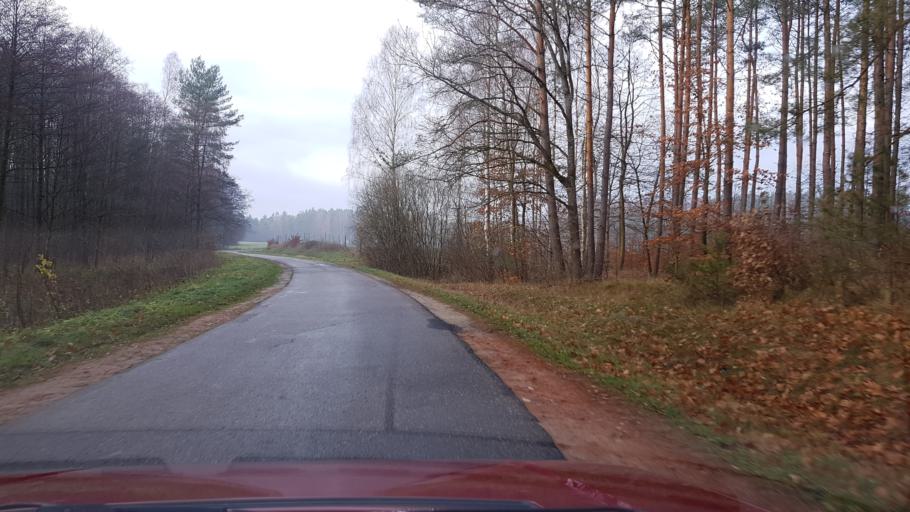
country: PL
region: West Pomeranian Voivodeship
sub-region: Powiat bialogardzki
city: Tychowo
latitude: 53.9454
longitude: 16.3198
